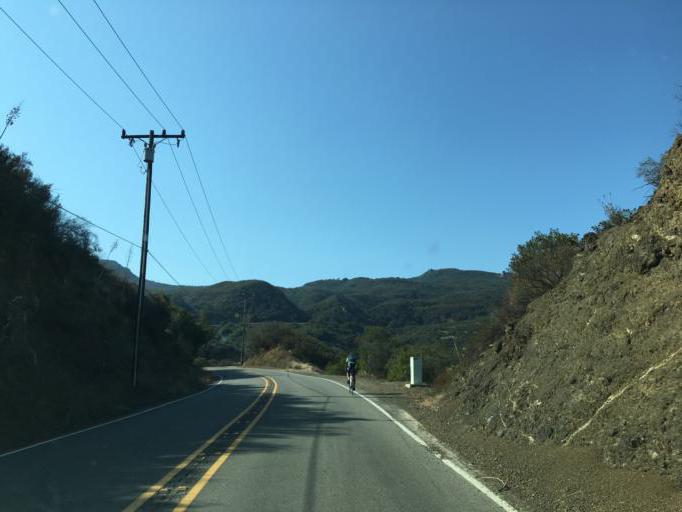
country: US
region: California
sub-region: Los Angeles County
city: Topanga
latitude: 34.0994
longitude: -118.6536
